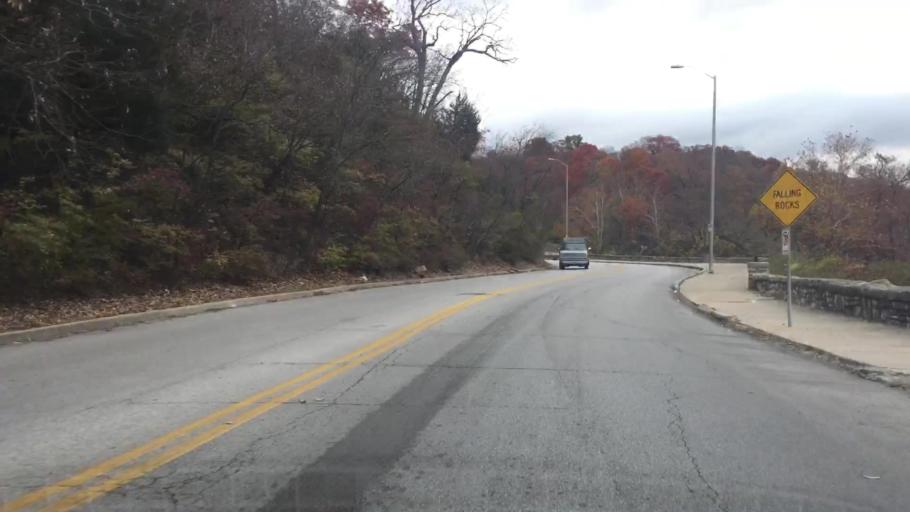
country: US
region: Missouri
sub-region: Jackson County
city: Raytown
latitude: 38.9962
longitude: -94.5205
